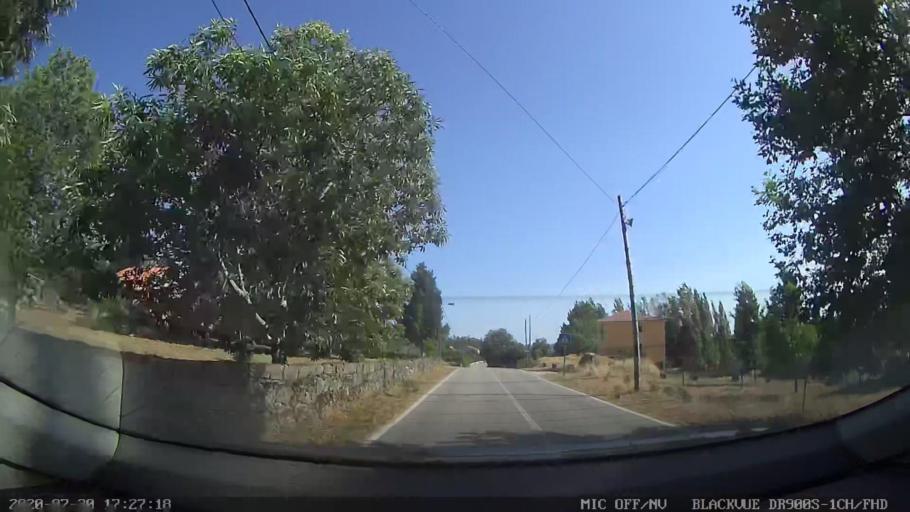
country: PT
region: Vila Real
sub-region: Murca
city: Murca
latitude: 41.3239
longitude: -7.4617
